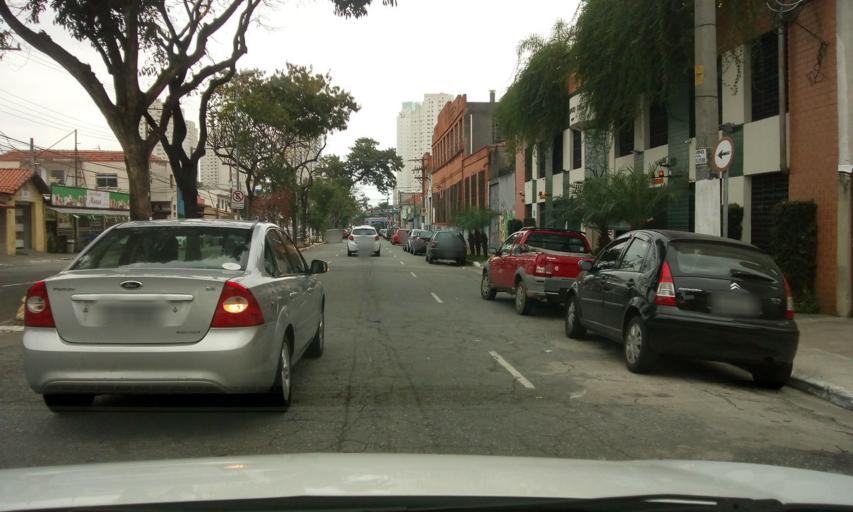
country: BR
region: Sao Paulo
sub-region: Sao Paulo
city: Sao Paulo
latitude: -23.5551
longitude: -46.5897
